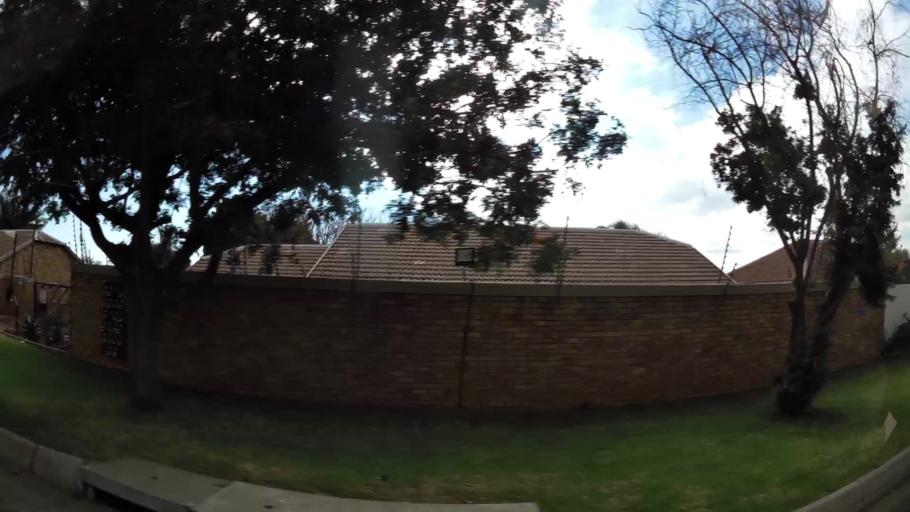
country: ZA
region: Gauteng
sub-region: City of Johannesburg Metropolitan Municipality
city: Roodepoort
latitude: -26.0978
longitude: 27.8681
